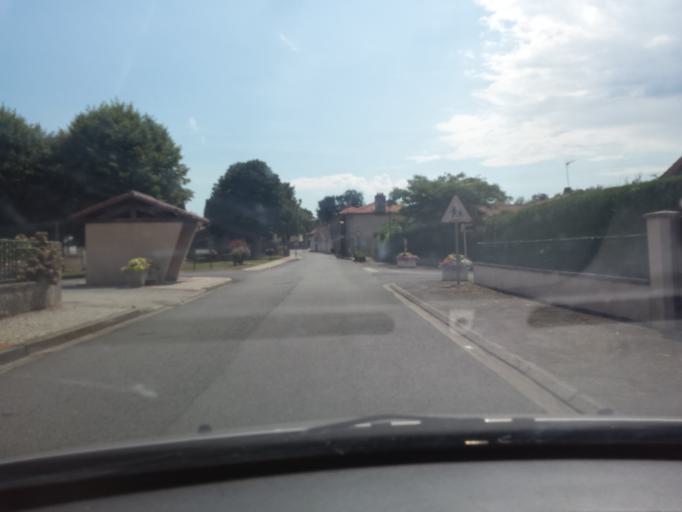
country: FR
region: Poitou-Charentes
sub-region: Departement de la Vienne
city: Availles-Limouzine
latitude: 46.1025
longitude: 0.7051
